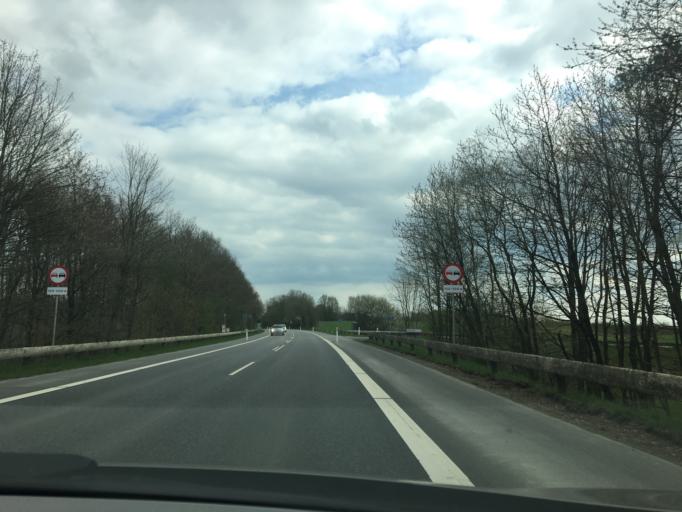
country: DK
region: Central Jutland
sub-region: Horsens Kommune
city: Braedstrup
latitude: 55.9549
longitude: 9.6245
